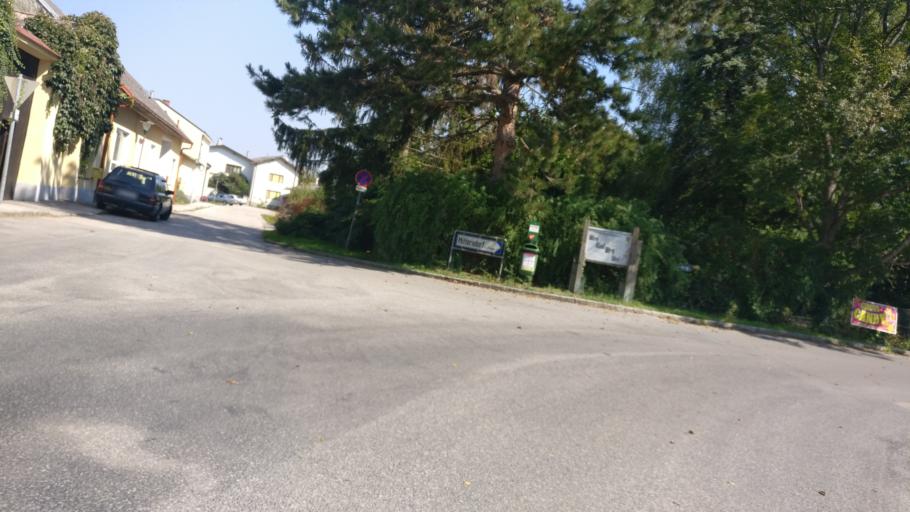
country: AT
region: Lower Austria
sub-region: Politischer Bezirk Baden
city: Mitterndorf an der Fischa
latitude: 47.9793
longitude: 16.4448
